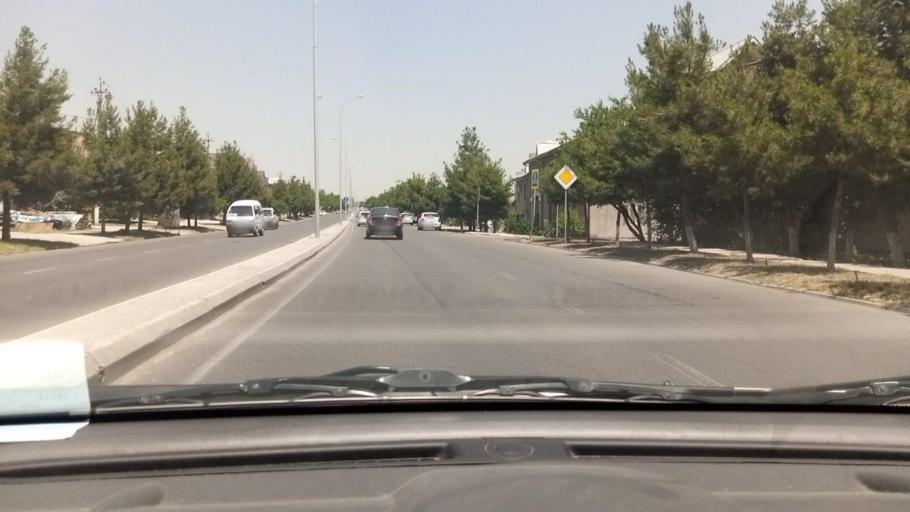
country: UZ
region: Toshkent Shahri
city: Tashkent
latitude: 41.2291
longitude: 69.1831
